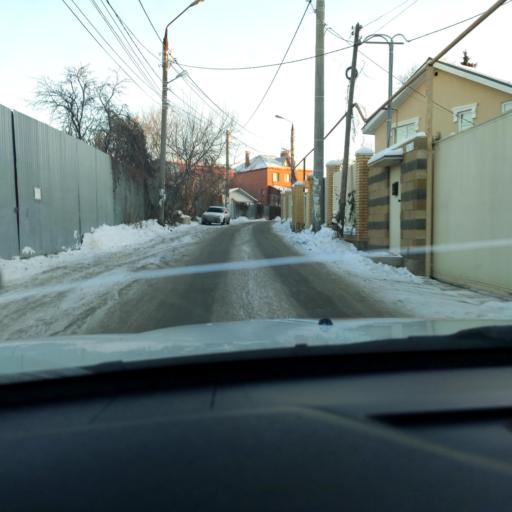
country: RU
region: Samara
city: Samara
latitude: 53.2574
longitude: 50.1851
